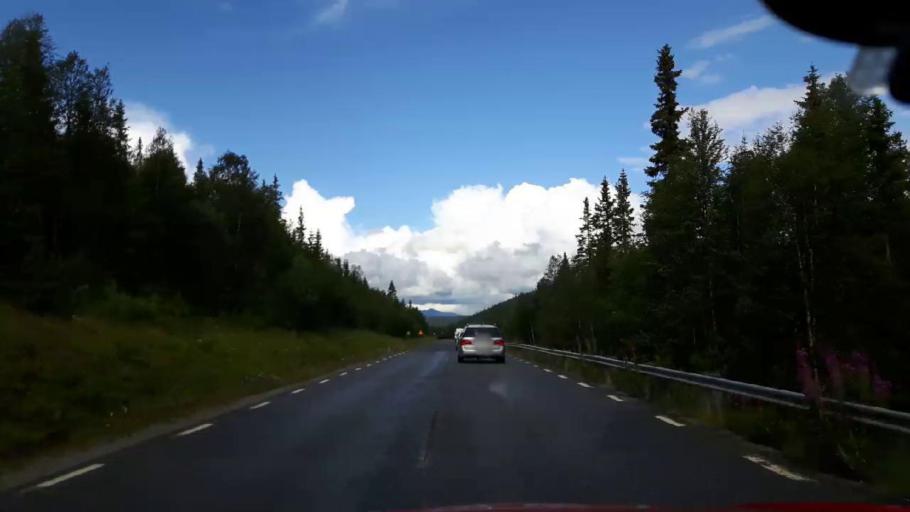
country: SE
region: Vaesterbotten
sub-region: Vilhelmina Kommun
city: Sjoberg
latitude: 65.0282
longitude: 15.1443
